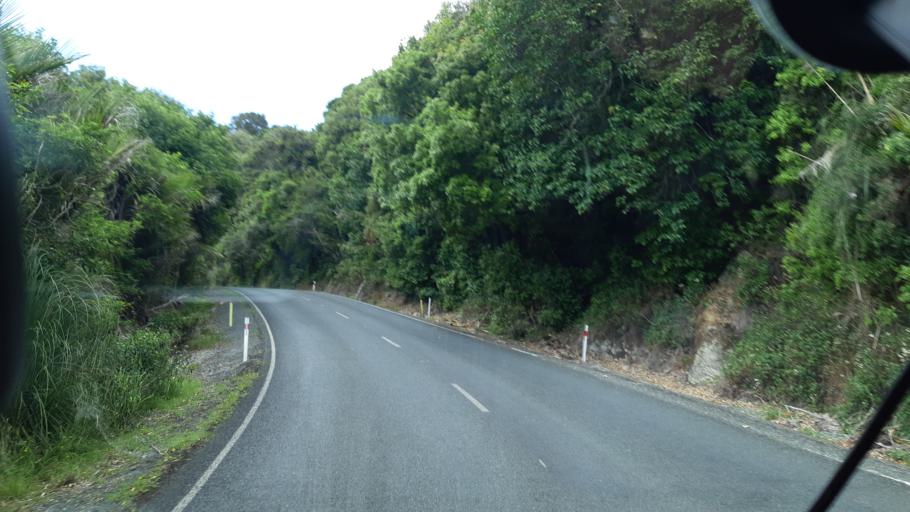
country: NZ
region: Northland
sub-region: Far North District
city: Taipa
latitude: -35.2467
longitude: 173.5309
